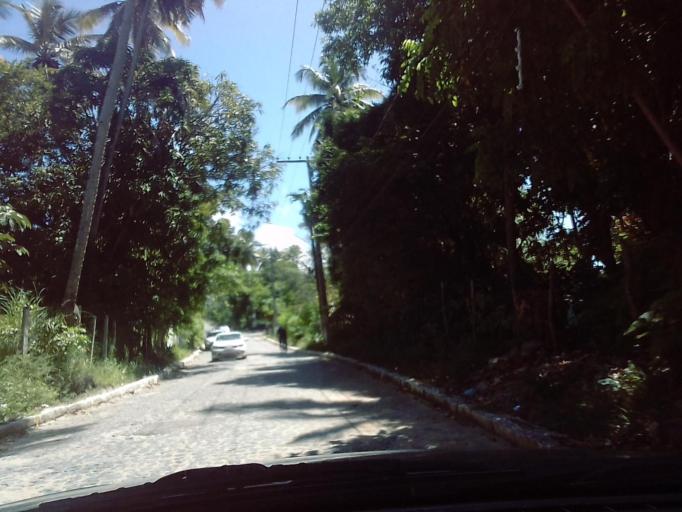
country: BR
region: Pernambuco
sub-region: Igarassu
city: Igarassu
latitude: -7.8434
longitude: -34.8452
